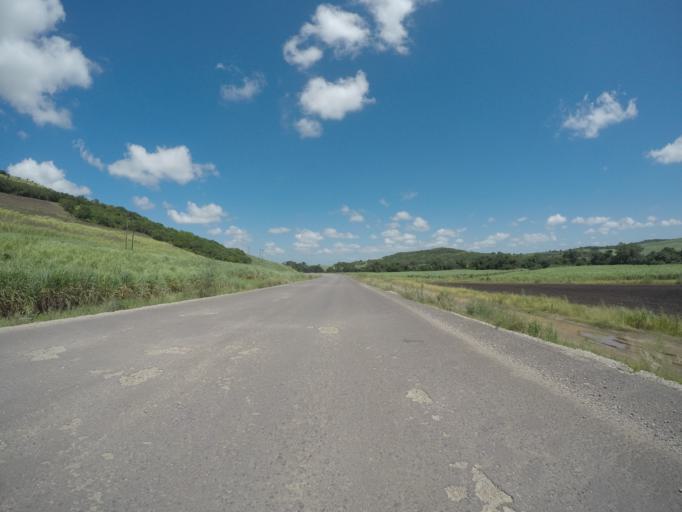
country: ZA
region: KwaZulu-Natal
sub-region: uThungulu District Municipality
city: Empangeni
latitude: -28.6519
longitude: 31.7689
